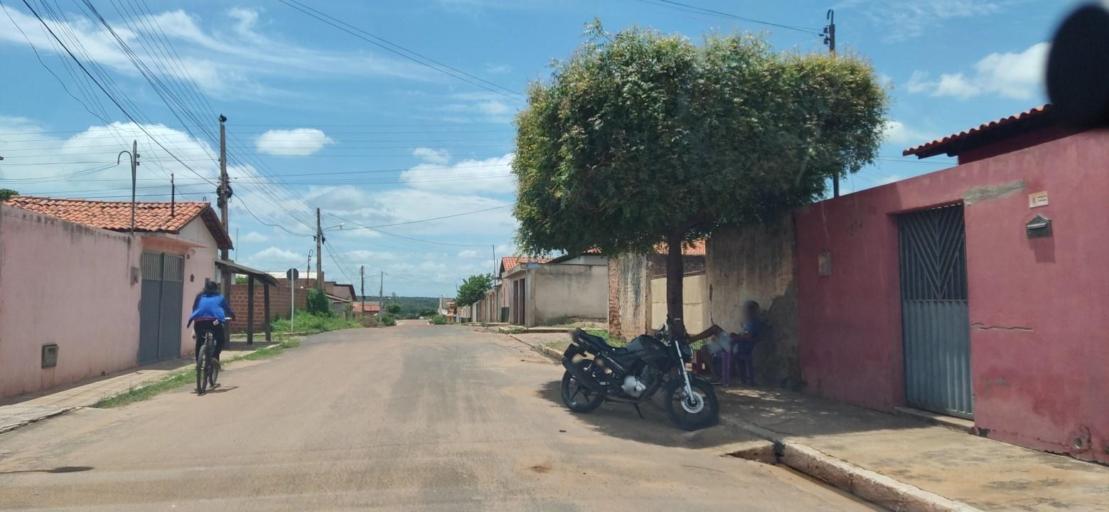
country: BR
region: Piaui
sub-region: Valenca Do Piaui
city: Valenca do Piaui
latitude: -6.4088
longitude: -41.7320
